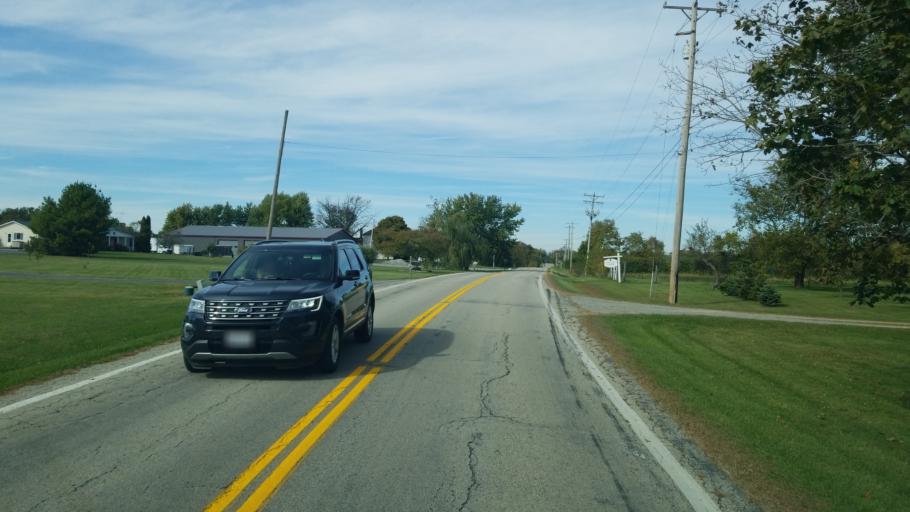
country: US
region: Ohio
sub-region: Highland County
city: Leesburg
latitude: 39.3286
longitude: -83.5907
